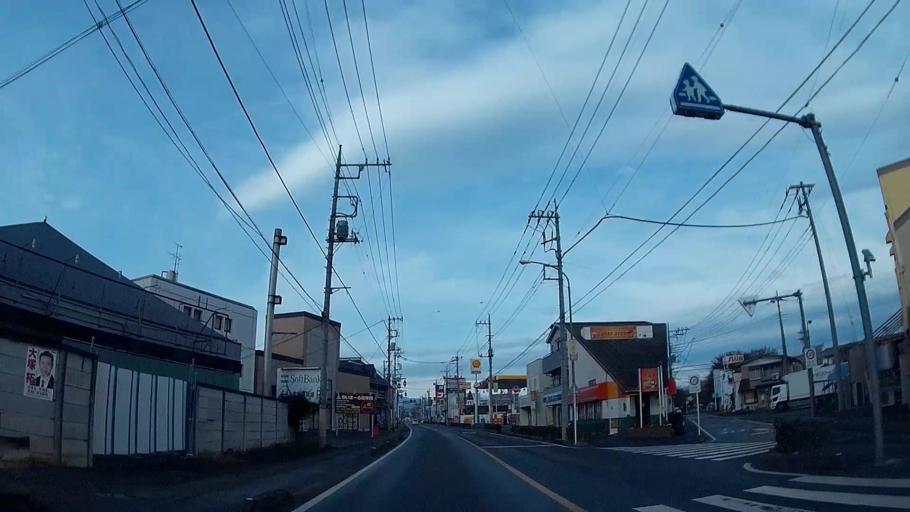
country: JP
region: Saitama
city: Hanno
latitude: 35.8488
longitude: 139.3330
